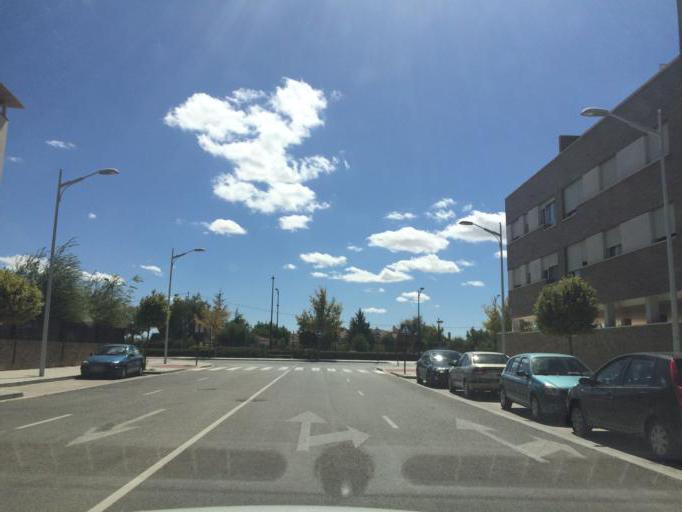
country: ES
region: Castille-La Mancha
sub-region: Provincia de Albacete
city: Albacete
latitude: 38.9783
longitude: -1.8410
